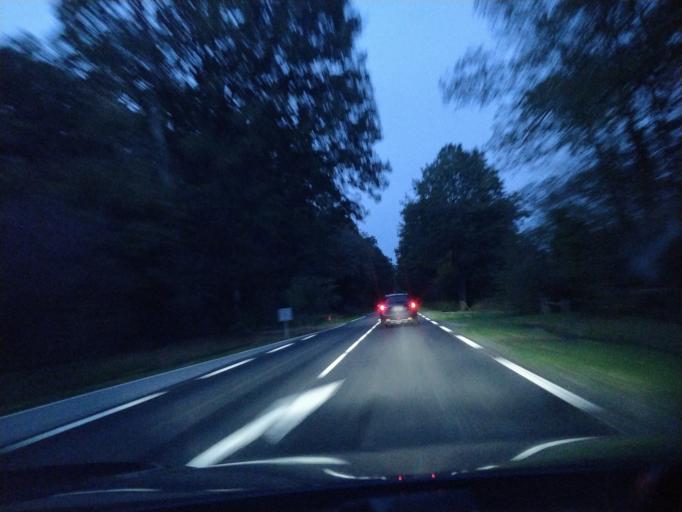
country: FR
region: Ile-de-France
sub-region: Departement des Yvelines
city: Bullion
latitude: 48.5964
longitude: 1.9981
